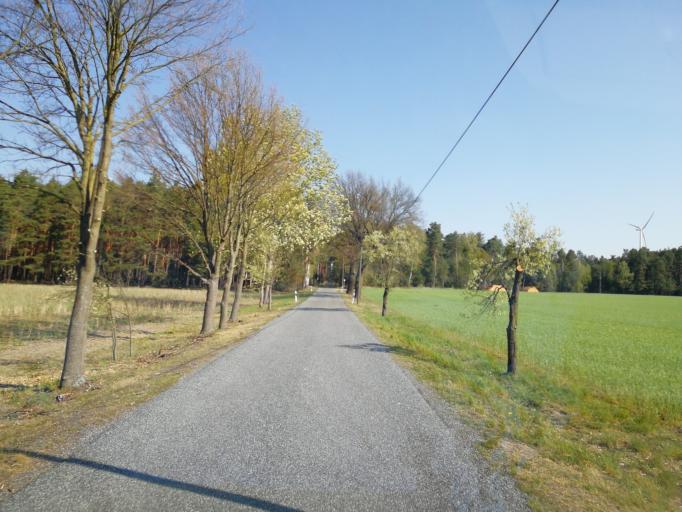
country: DE
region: Brandenburg
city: Bronkow
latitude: 51.6690
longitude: 13.8639
